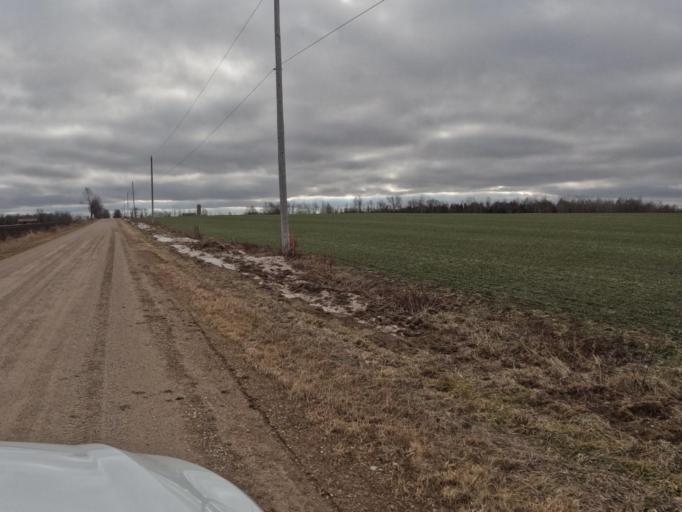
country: CA
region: Ontario
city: Shelburne
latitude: 43.8951
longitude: -80.4074
